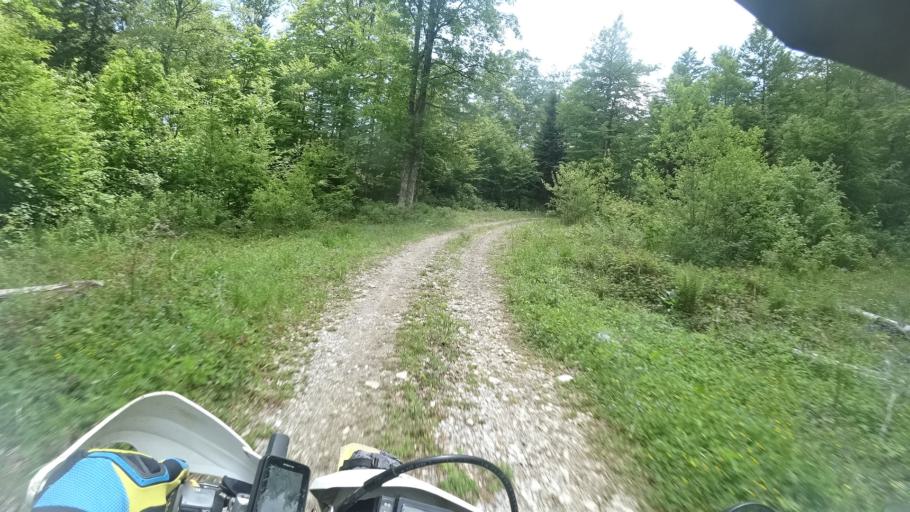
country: HR
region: Zadarska
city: Gracac
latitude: 44.4702
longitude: 15.8927
